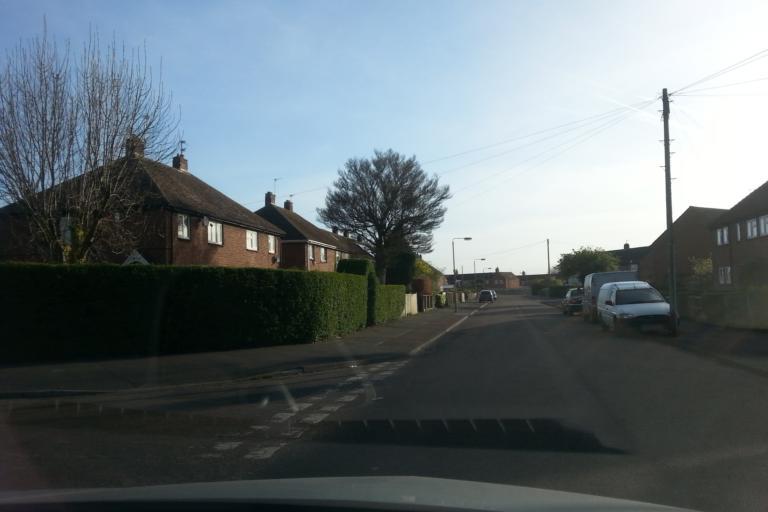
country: GB
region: England
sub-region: Nottinghamshire
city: Newark on Trent
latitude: 53.0618
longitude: -0.8155
